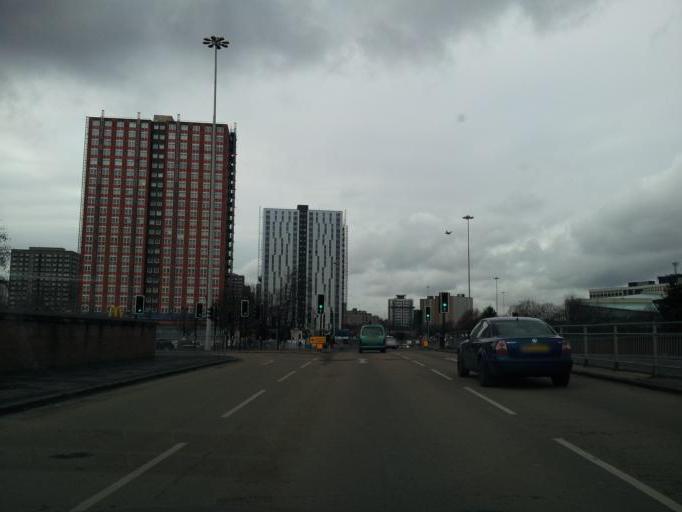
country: GB
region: England
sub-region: City and Borough of Salford
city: Salford
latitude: 53.4853
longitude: -2.2755
